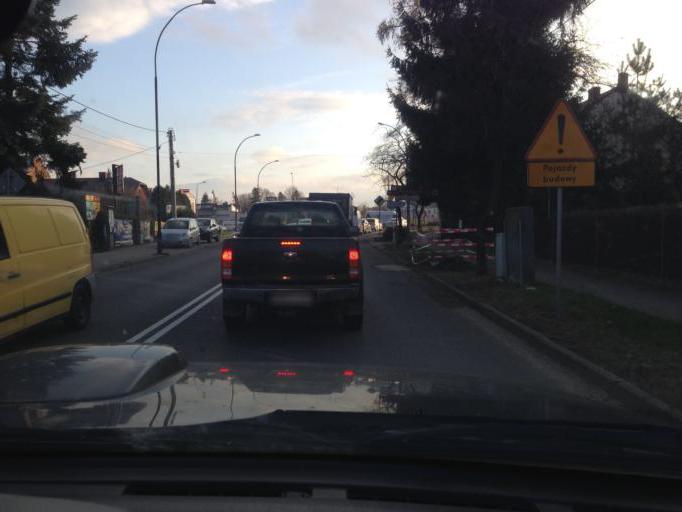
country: PL
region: Subcarpathian Voivodeship
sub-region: Powiat jasielski
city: Jaslo
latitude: 49.7532
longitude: 21.4738
